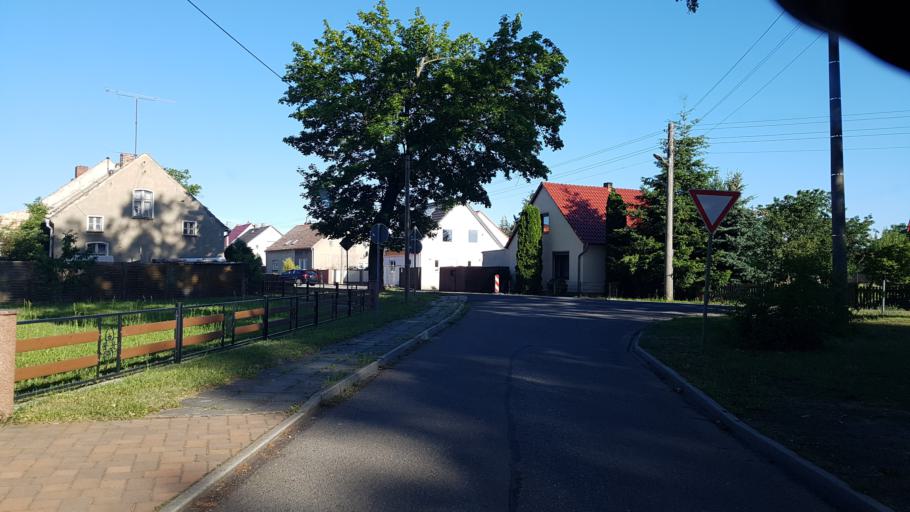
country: DE
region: Brandenburg
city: Drahnsdorf
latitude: 51.8172
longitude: 13.5992
